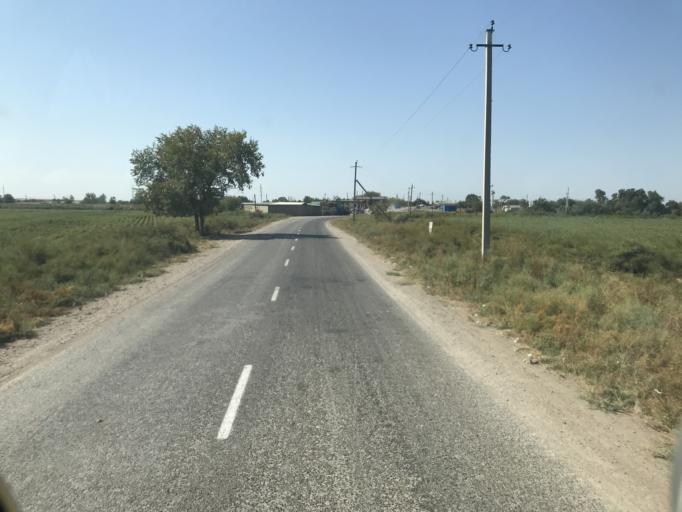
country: KZ
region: Ongtustik Qazaqstan
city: Myrzakent
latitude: 40.6720
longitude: 68.5529
